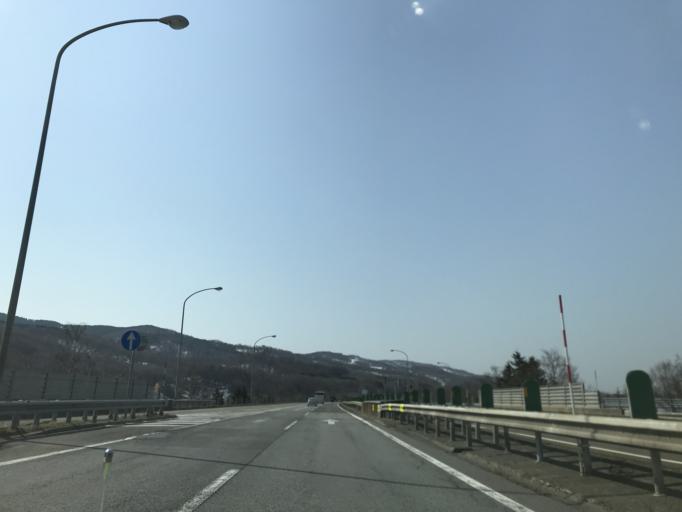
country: JP
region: Hokkaido
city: Bibai
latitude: 43.3322
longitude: 141.8883
